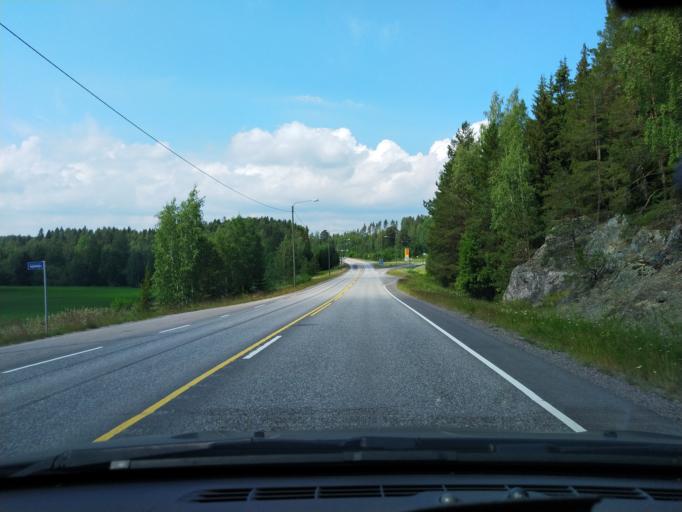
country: FI
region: Uusimaa
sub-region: Helsinki
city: Saukkola
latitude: 60.3823
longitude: 24.0880
